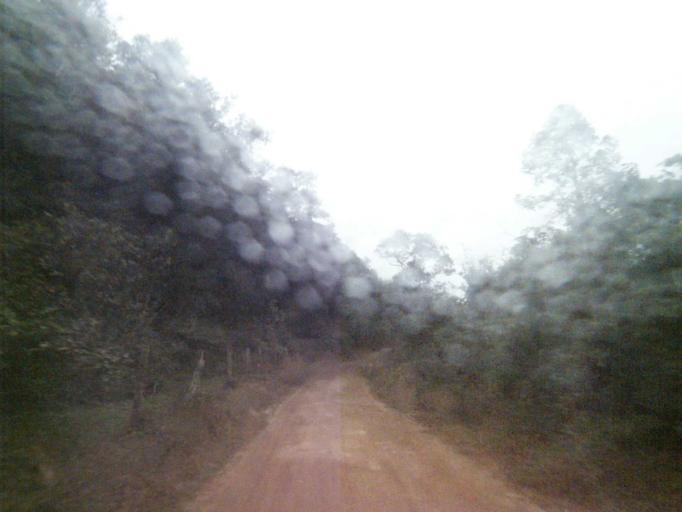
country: BR
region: Santa Catarina
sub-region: Anitapolis
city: Anitapolis
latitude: -27.8702
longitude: -49.1307
